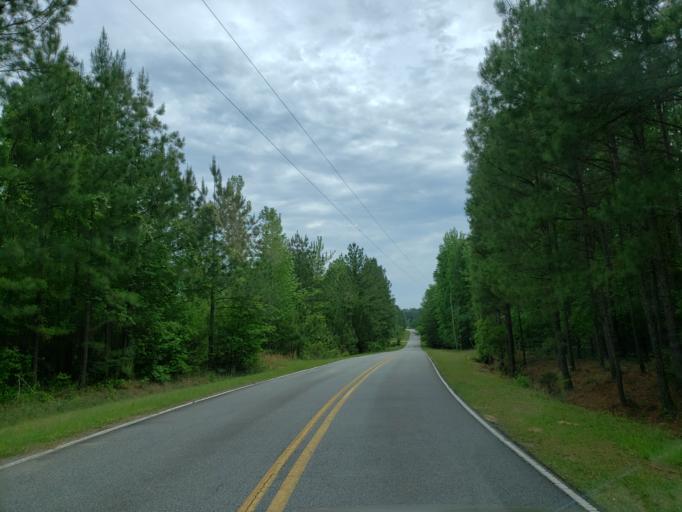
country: US
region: Georgia
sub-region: Bibb County
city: West Point
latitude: 32.8479
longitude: -83.8891
